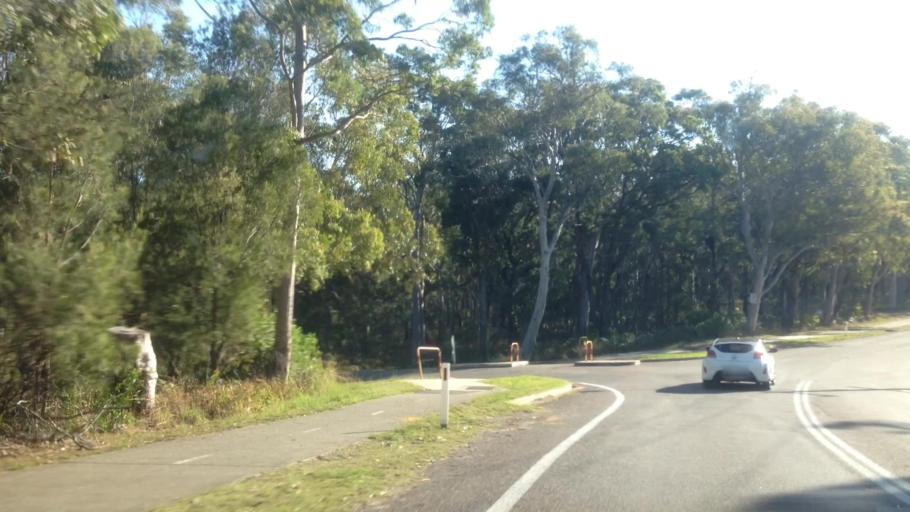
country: AU
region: New South Wales
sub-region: Lake Macquarie Shire
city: Dora Creek
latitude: -33.1122
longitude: 151.5288
